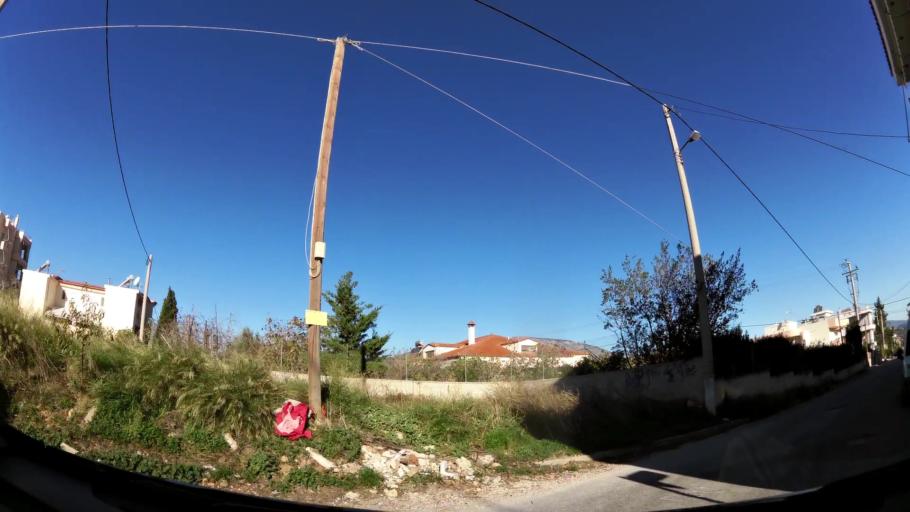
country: GR
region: Attica
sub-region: Nomarchia Anatolikis Attikis
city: Koropi
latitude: 37.8968
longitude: 23.8623
